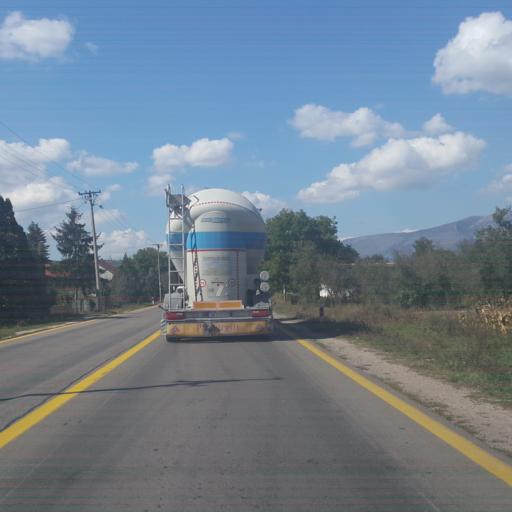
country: RS
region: Central Serbia
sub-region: Pirotski Okrug
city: Bela Palanka
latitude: 43.2652
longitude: 22.2503
